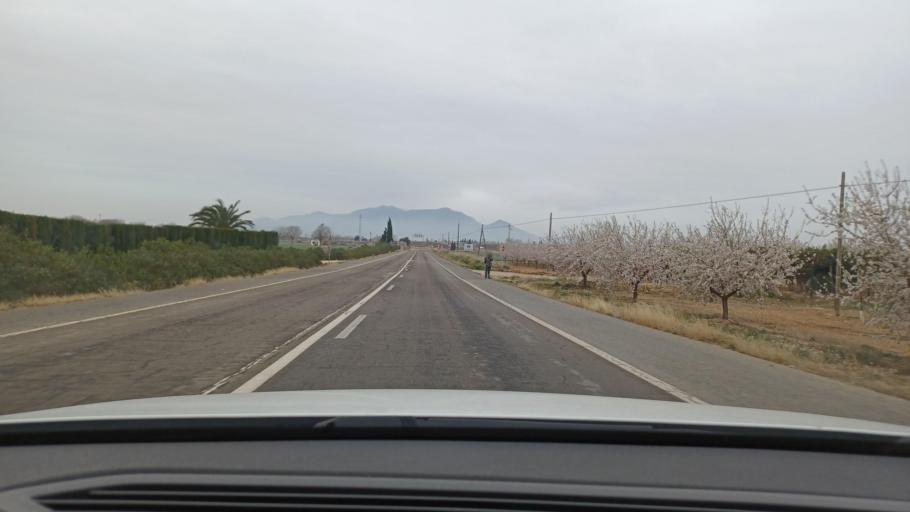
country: ES
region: Catalonia
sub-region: Provincia de Tarragona
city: Amposta
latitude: 40.7329
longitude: 0.5950
